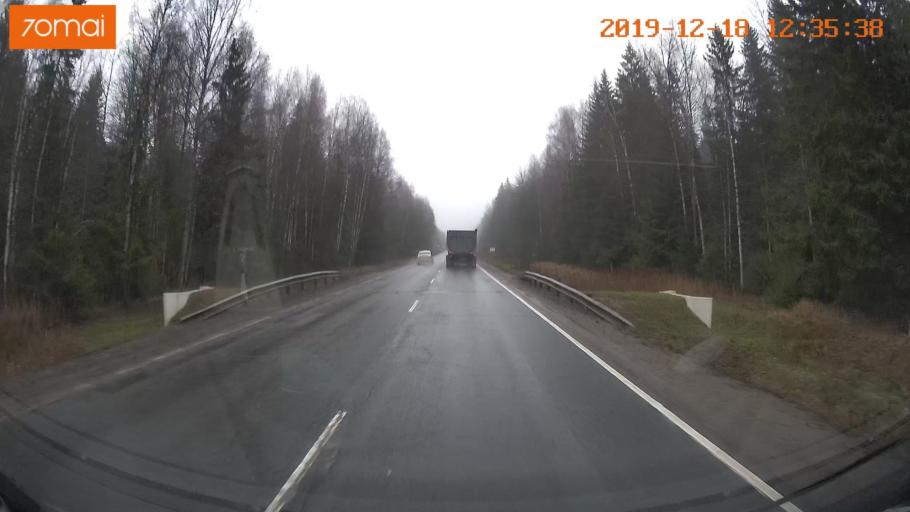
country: RU
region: Moskovskaya
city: Rumyantsevo
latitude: 56.1312
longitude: 36.5857
